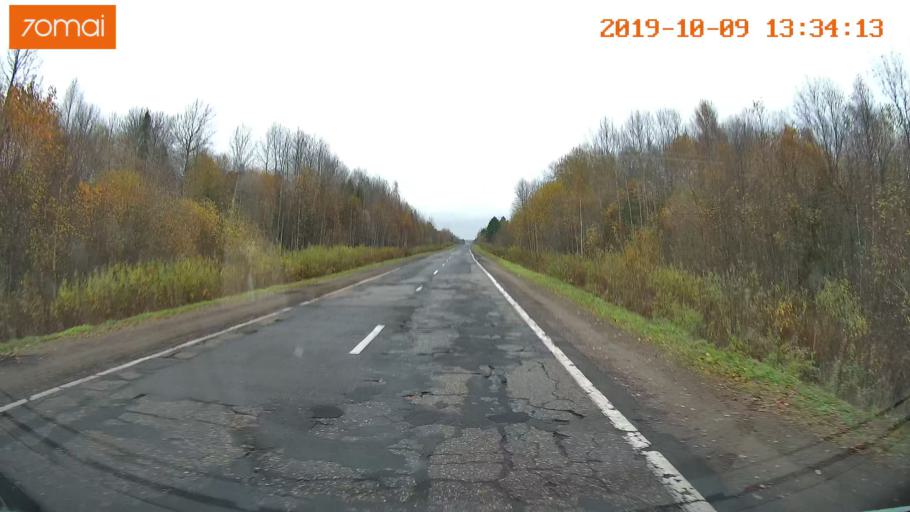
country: RU
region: Jaroslavl
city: Lyubim
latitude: 58.3291
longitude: 41.0580
